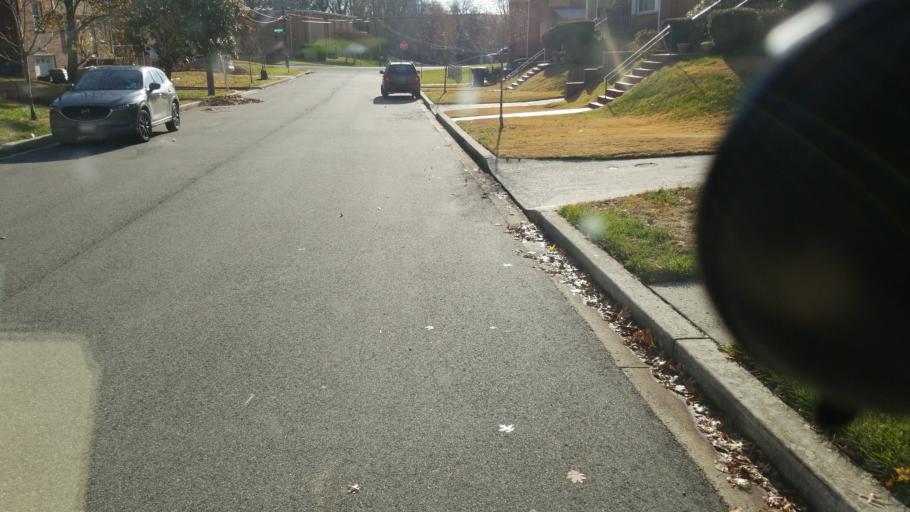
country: US
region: Maryland
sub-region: Prince George's County
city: Silver Hill
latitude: 38.8589
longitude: -76.9544
